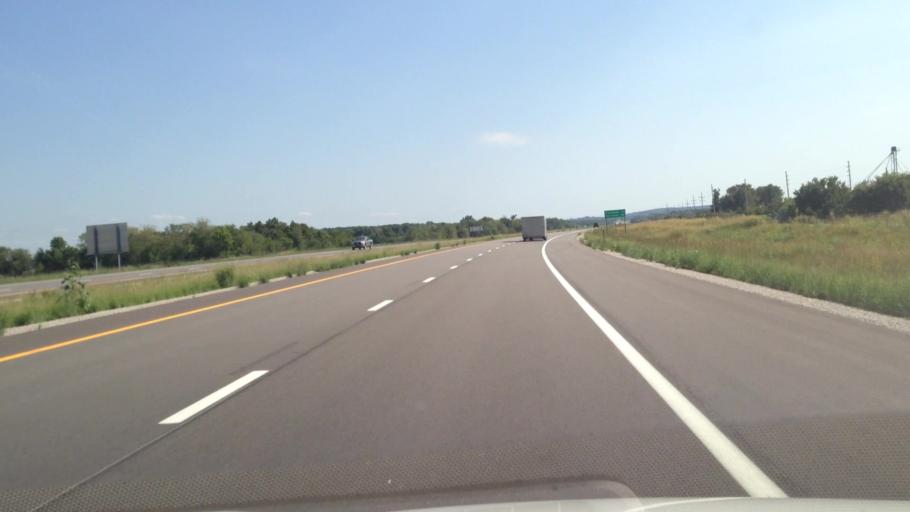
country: US
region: Kansas
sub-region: Linn County
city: La Cygne
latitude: 38.3335
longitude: -94.6780
